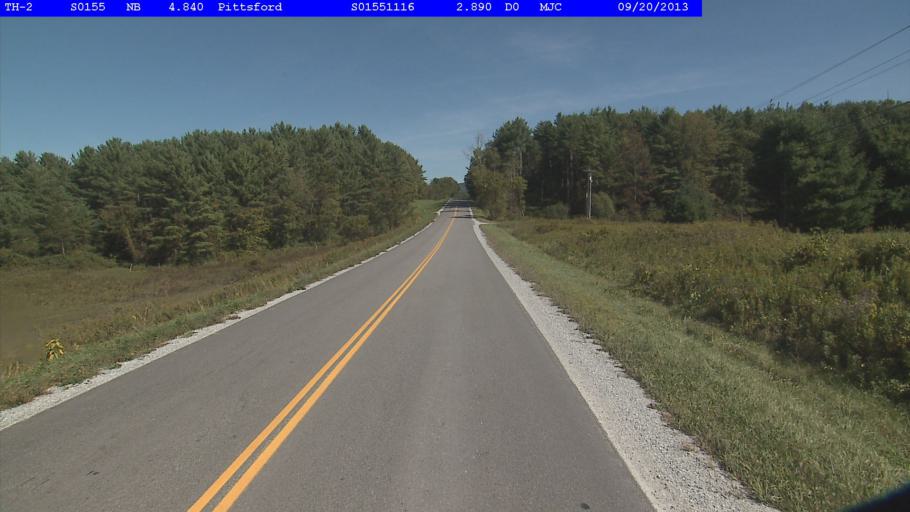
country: US
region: Vermont
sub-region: Rutland County
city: Brandon
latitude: 43.7198
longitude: -73.0487
